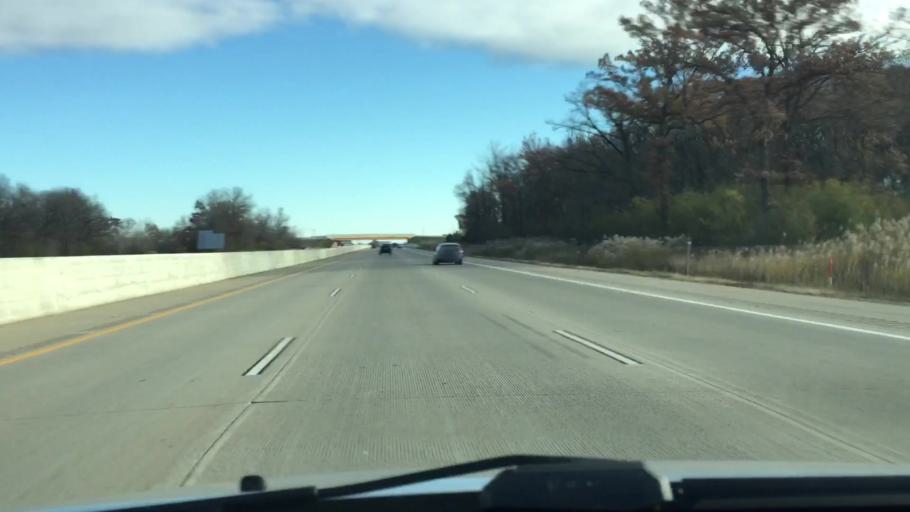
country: US
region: Wisconsin
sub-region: Winnebago County
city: Oshkosh
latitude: 44.1085
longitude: -88.5263
